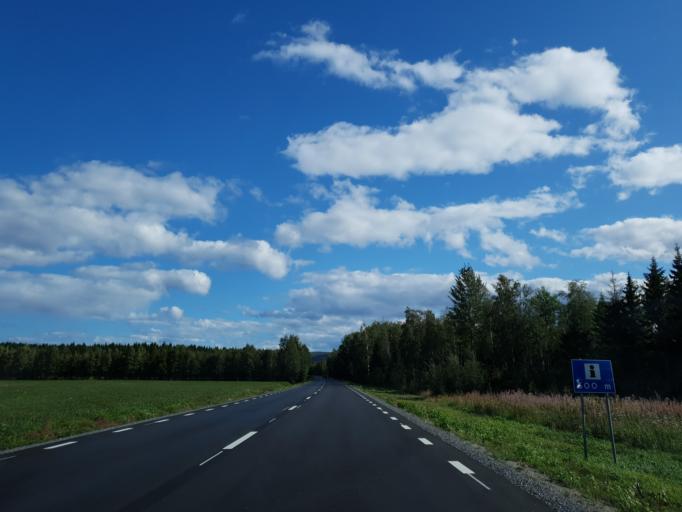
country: SE
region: Vaesternorrland
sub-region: OErnskoeldsviks Kommun
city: Bjasta
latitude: 63.1886
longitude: 18.5150
